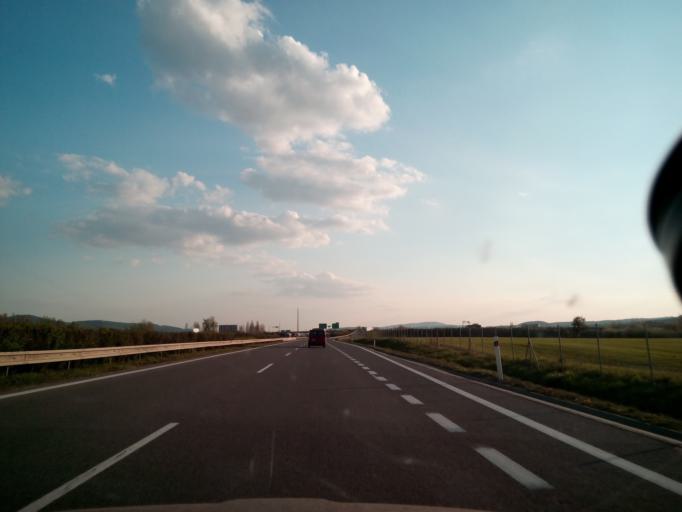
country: SK
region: Trenciansky
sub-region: Okres Trencin
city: Trencin
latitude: 48.8653
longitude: 17.9640
